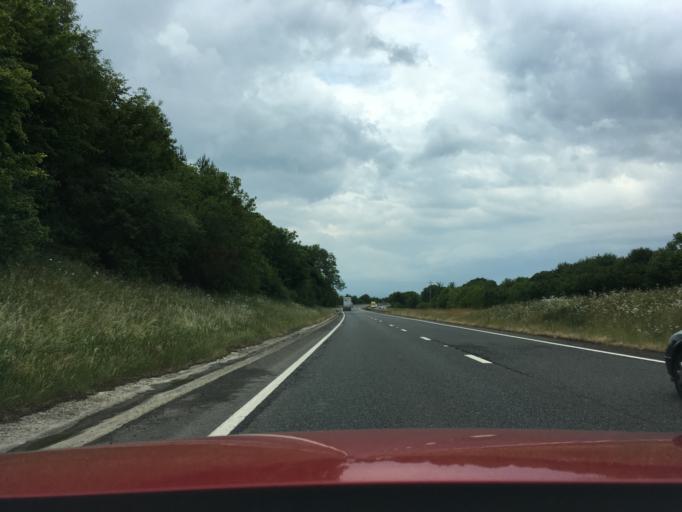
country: GB
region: England
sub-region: Gloucestershire
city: Coates
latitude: 51.7788
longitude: -2.0330
